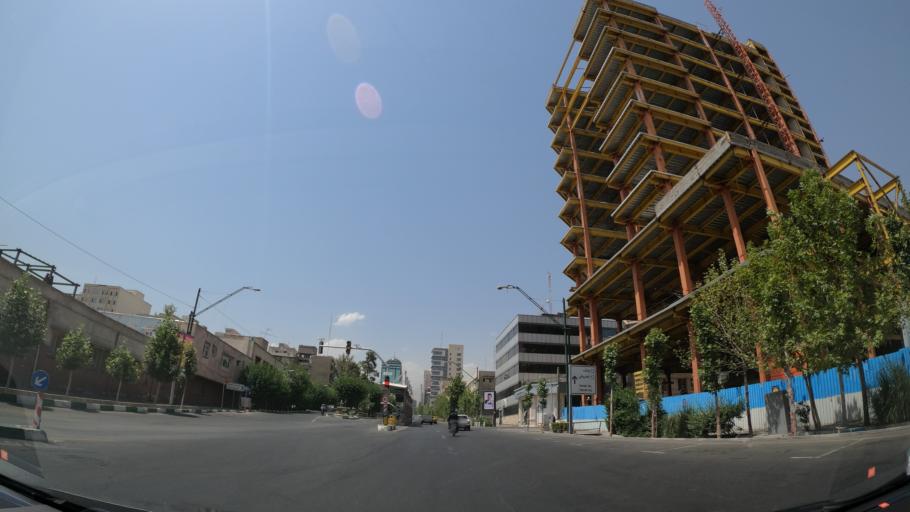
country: IR
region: Tehran
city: Tehran
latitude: 35.7275
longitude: 51.4134
